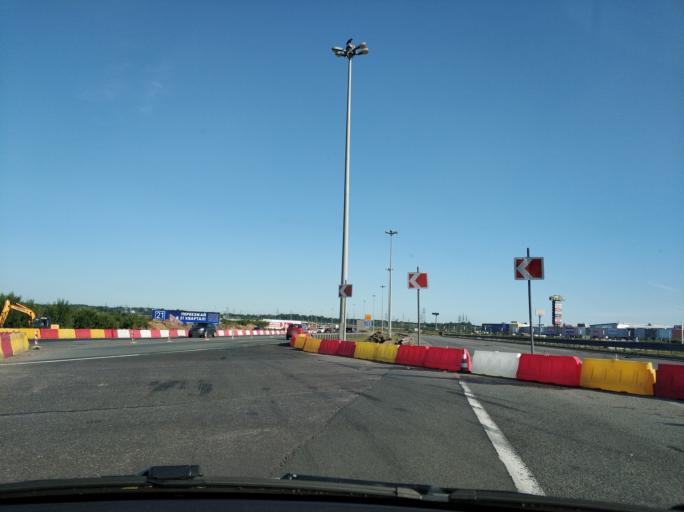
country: RU
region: Leningrad
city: Bugry
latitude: 60.0839
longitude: 30.3786
